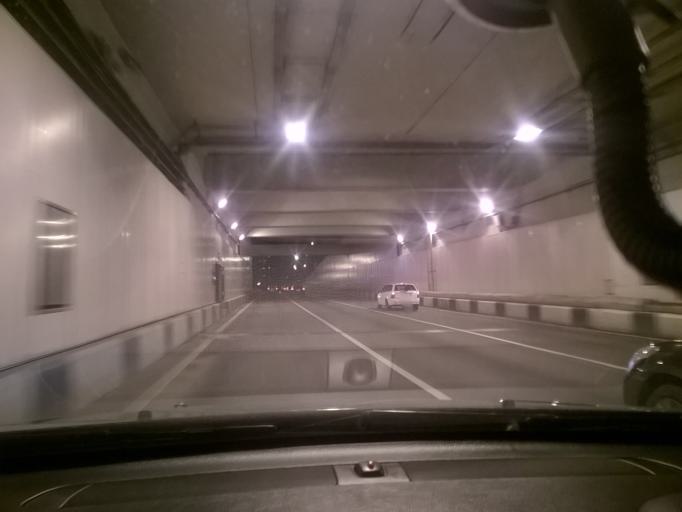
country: RU
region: Moskovskaya
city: Koptevo
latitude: 55.8127
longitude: 37.5158
